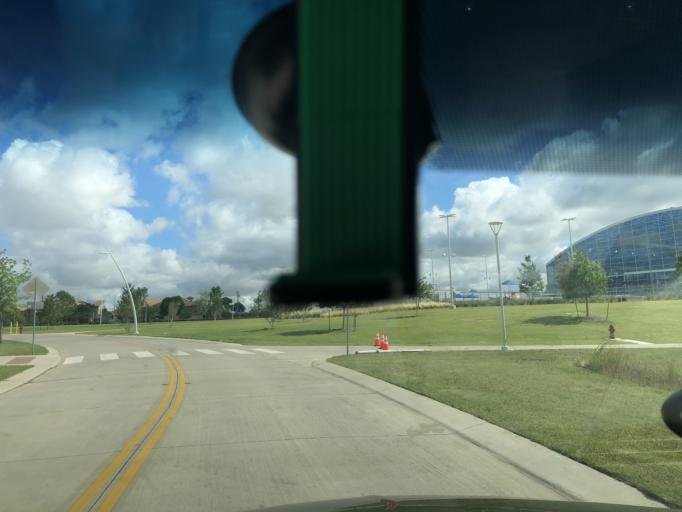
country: US
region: Texas
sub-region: Dallas County
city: Grand Prairie
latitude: 32.7010
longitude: -97.0329
